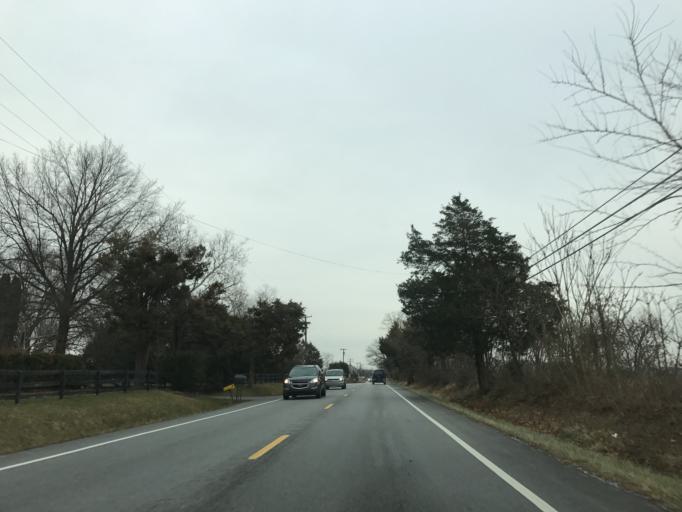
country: US
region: Maryland
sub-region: Carroll County
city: Taneytown
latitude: 39.6736
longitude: -77.2115
